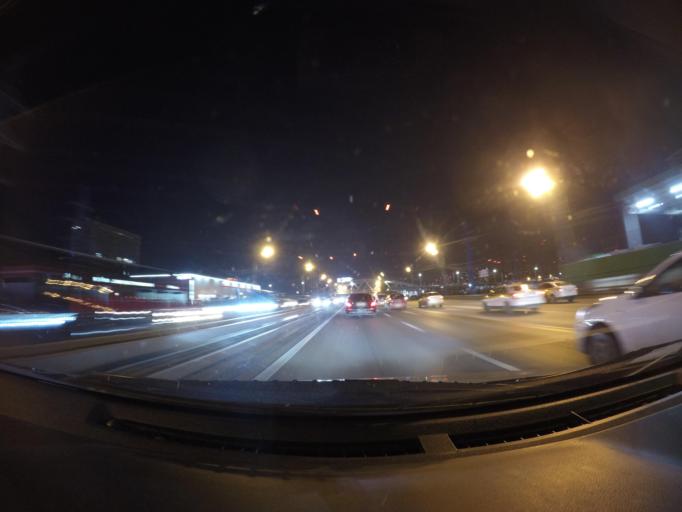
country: RU
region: Moscow
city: Khimki
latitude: 55.9034
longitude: 37.4176
